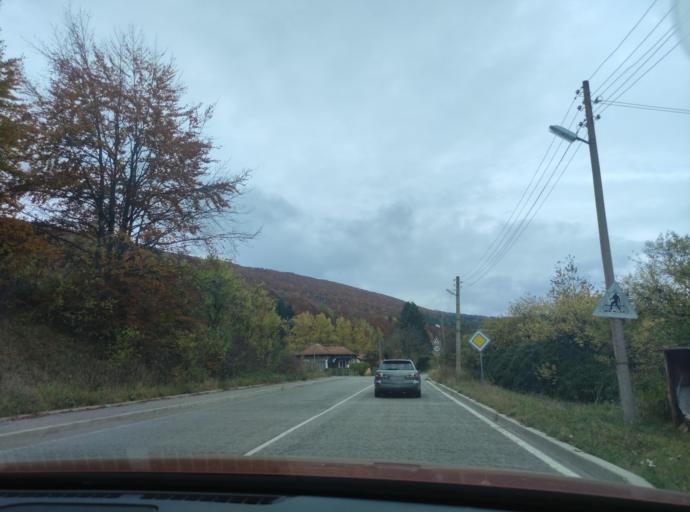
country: BG
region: Sofiya
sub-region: Obshtina Godech
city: Godech
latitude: 43.0874
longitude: 23.1003
